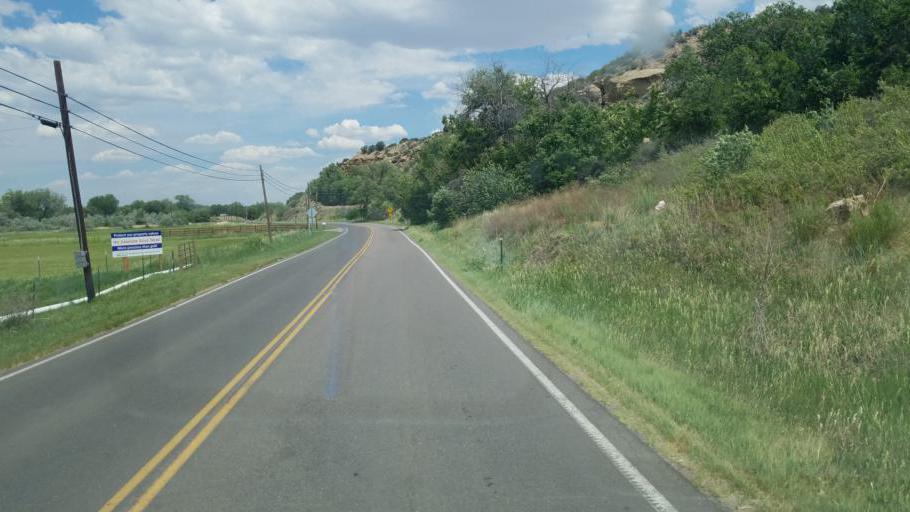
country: US
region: Colorado
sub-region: Fremont County
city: Florence
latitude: 38.4042
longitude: -105.1538
